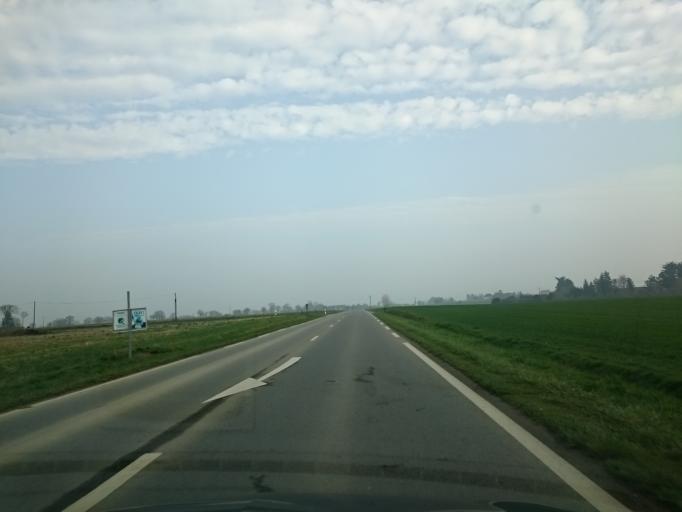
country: FR
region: Brittany
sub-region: Departement d'Ille-et-Vilaine
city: Chatillon-sur-Seiche
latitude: 48.0493
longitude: -1.6648
